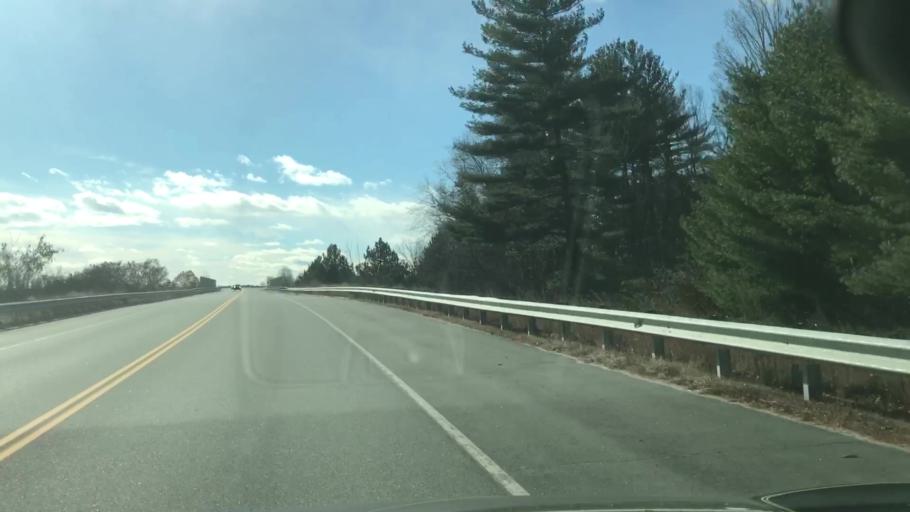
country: US
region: New Hampshire
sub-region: Merrimack County
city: Chichester
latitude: 43.2359
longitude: -71.4655
